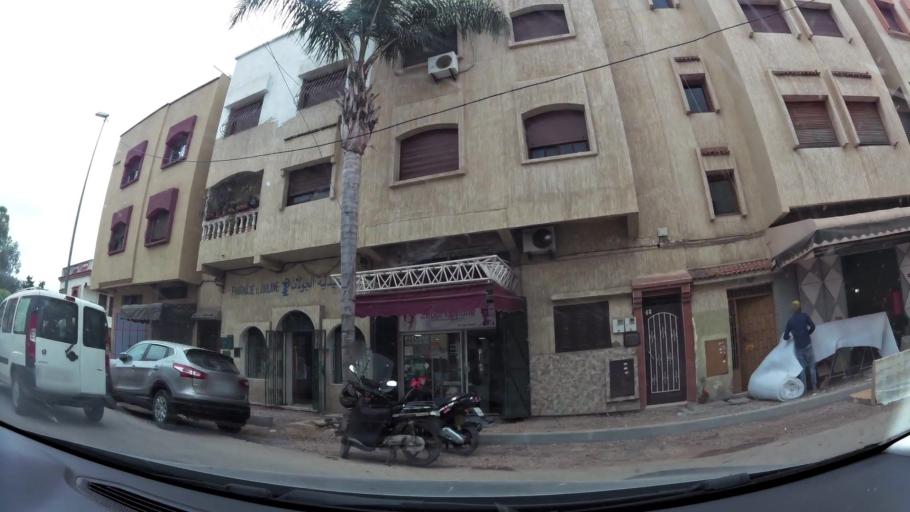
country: MA
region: Rabat-Sale-Zemmour-Zaer
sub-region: Rabat
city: Rabat
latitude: 33.9787
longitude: -6.8225
